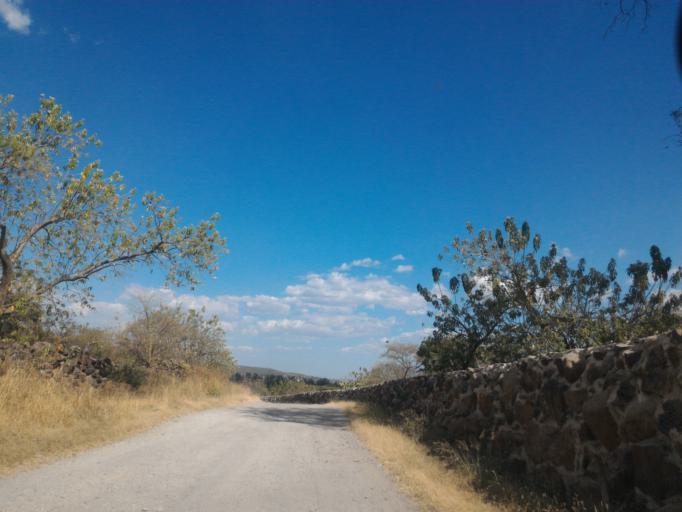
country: MX
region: Jalisco
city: San Diego de Alejandria
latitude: 20.8852
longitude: -101.9919
